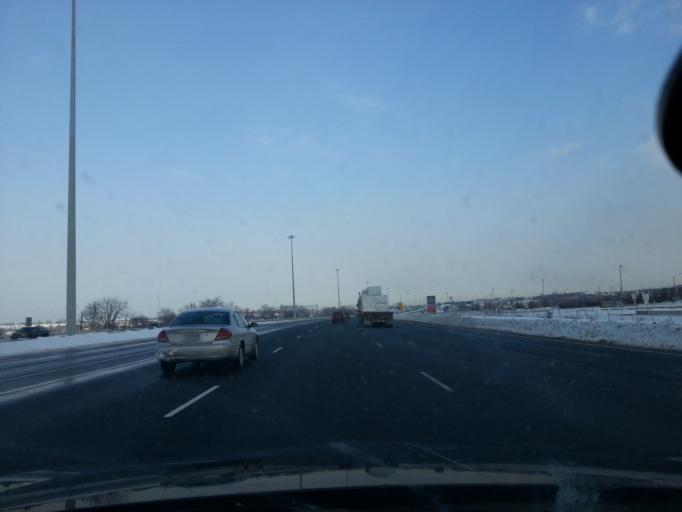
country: CA
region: Ontario
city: Bells Corners
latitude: 45.2975
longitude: -75.9310
